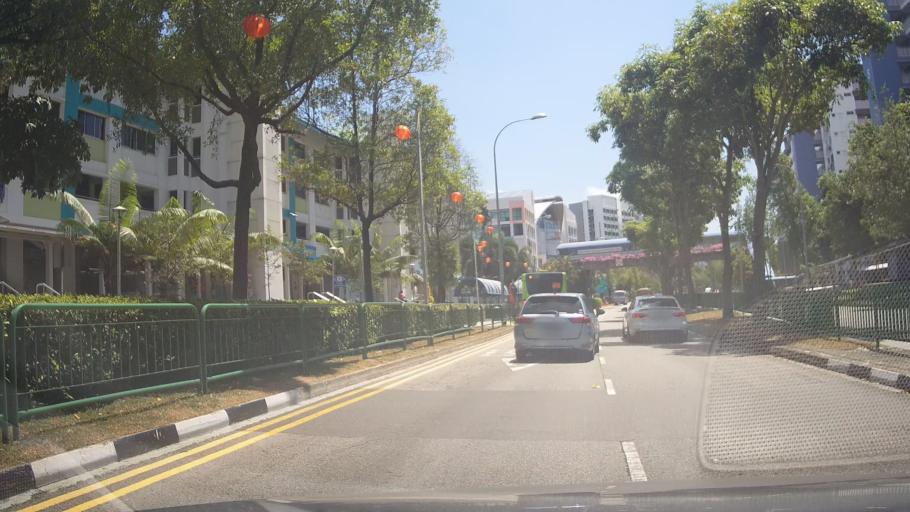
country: MY
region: Johor
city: Kampung Pasir Gudang Baru
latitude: 1.3689
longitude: 103.9573
